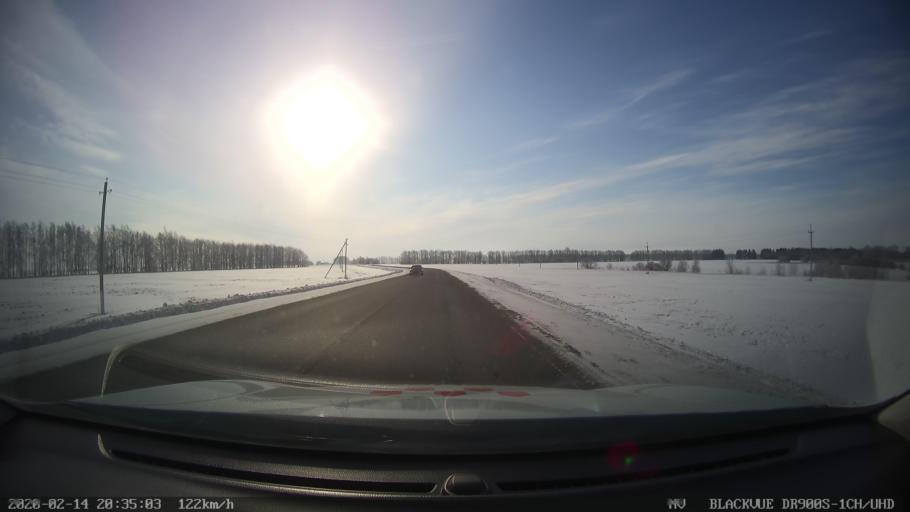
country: RU
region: Tatarstan
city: Kuybyshevskiy Zaton
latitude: 55.3883
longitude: 48.9799
